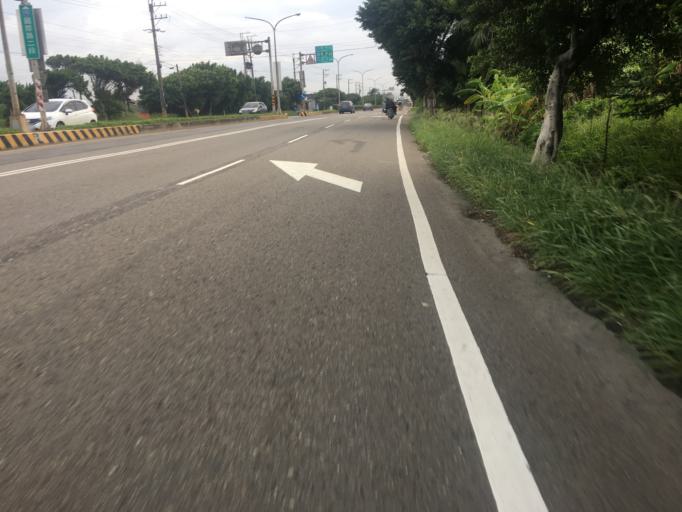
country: TW
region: Taiwan
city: Taoyuan City
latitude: 25.0939
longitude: 121.2331
